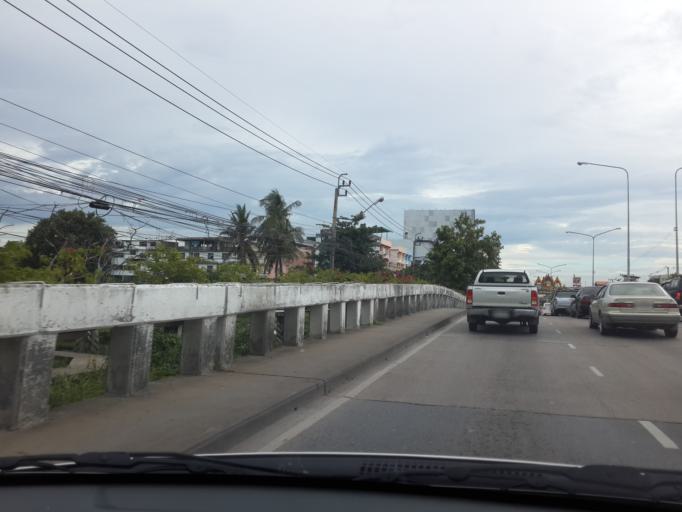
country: TH
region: Bangkok
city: Saphan Sung
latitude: 13.7901
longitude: 100.6977
